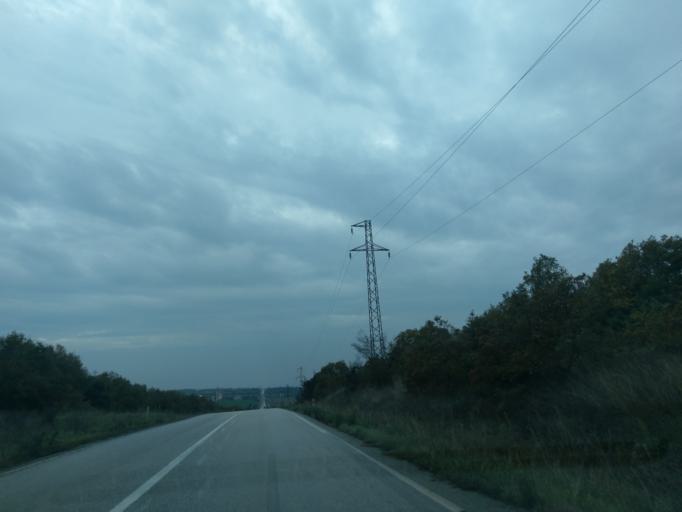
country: TR
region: Istanbul
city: Canta
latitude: 41.1546
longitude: 28.1068
